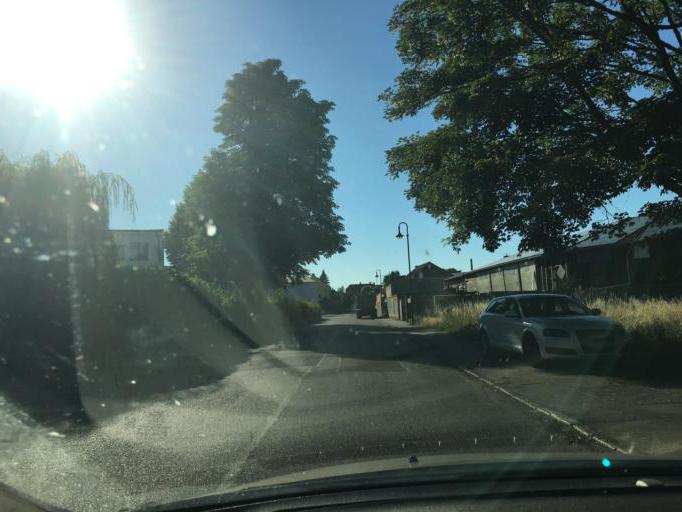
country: DE
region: Saxony
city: Grossposna
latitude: 51.2797
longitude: 12.4722
